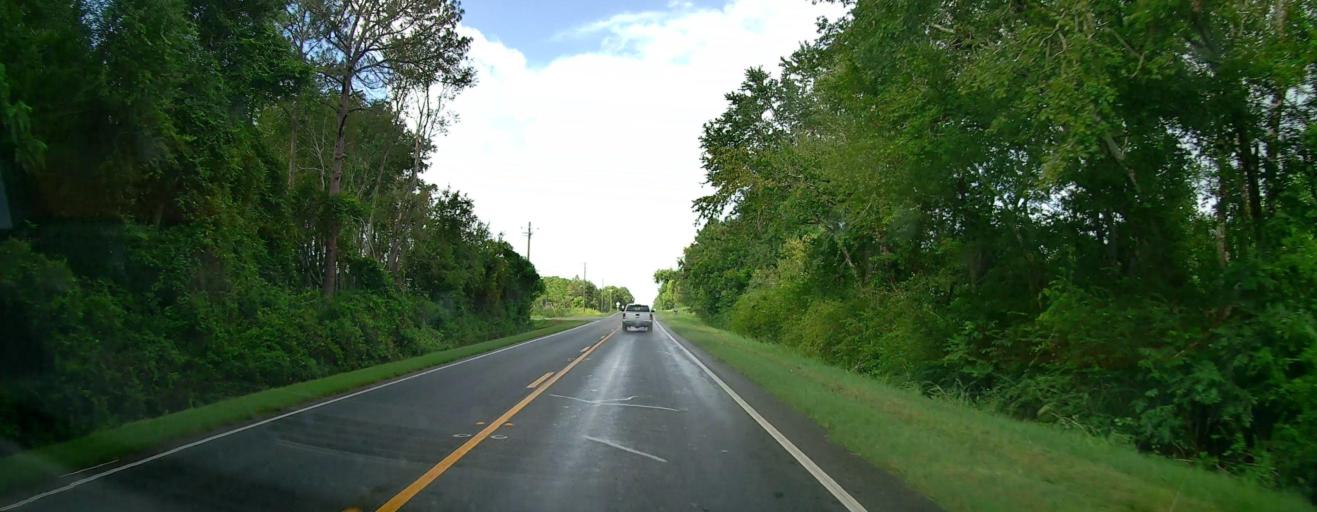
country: US
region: Georgia
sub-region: Coffee County
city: Douglas
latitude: 31.4795
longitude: -82.8685
